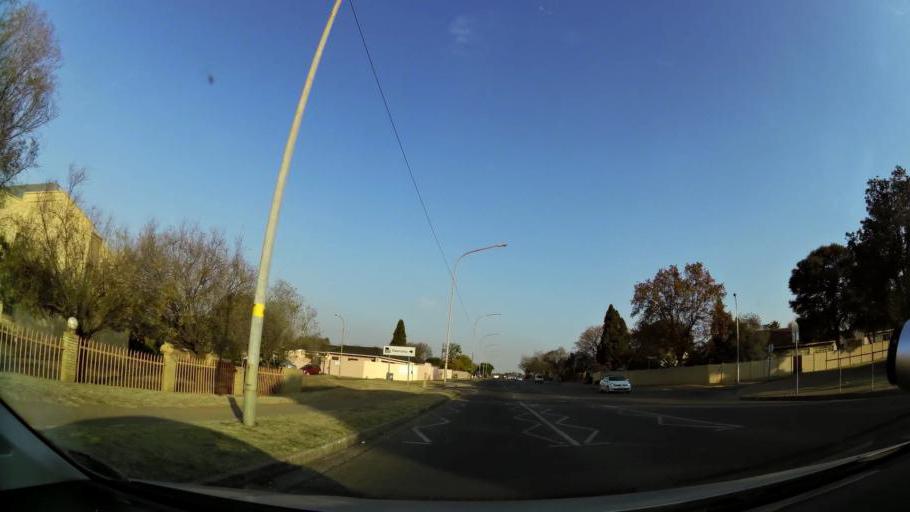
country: ZA
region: Gauteng
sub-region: City of Johannesburg Metropolitan Municipality
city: Modderfontein
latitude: -26.0862
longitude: 28.2137
